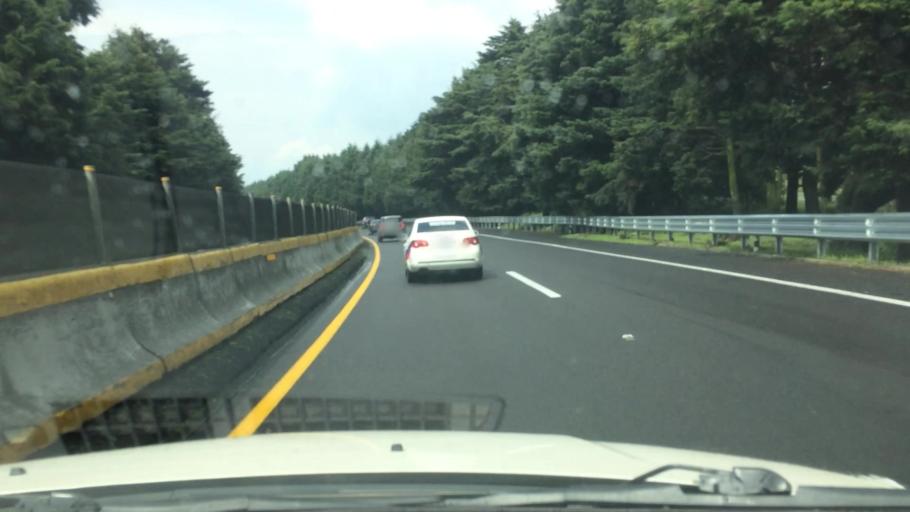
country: MX
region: Morelos
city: Tres Marias
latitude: 19.1348
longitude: -99.1672
